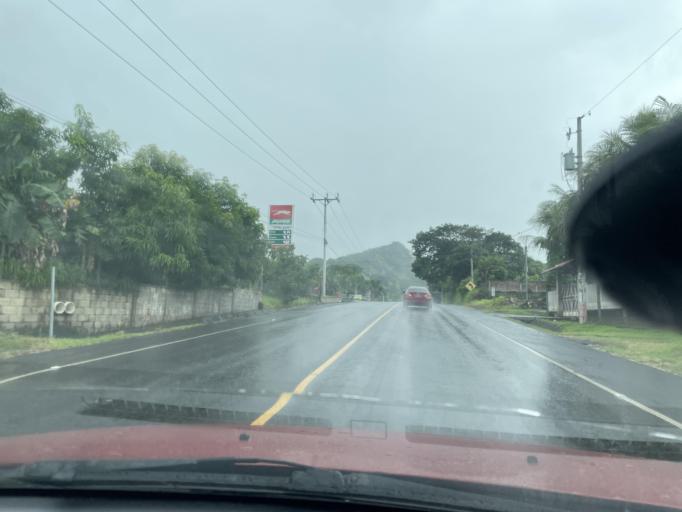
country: SV
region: Morazan
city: Jocoro
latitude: 13.5672
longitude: -88.0924
